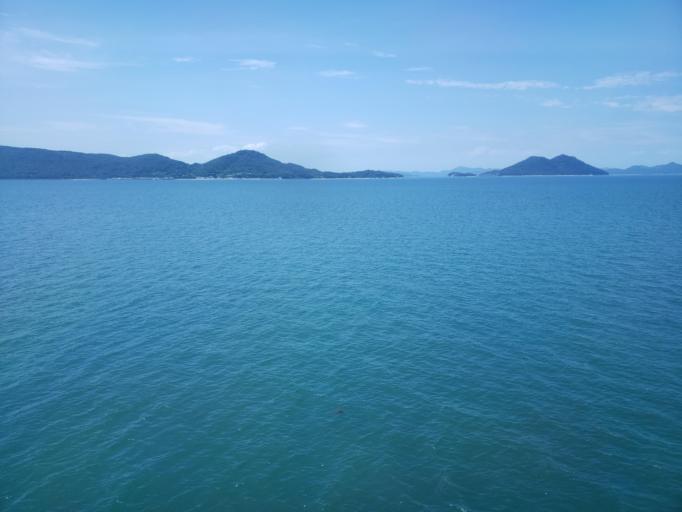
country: JP
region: Kagawa
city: Takamatsu-shi
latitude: 34.3761
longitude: 134.0817
